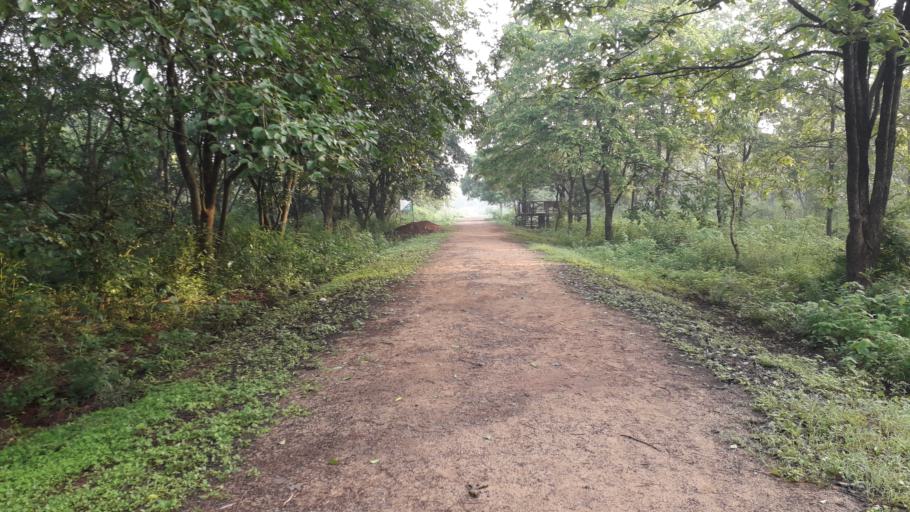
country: IN
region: Andhra Pradesh
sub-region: East Godavari
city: Rajahmundry
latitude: 17.0367
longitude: 81.8202
